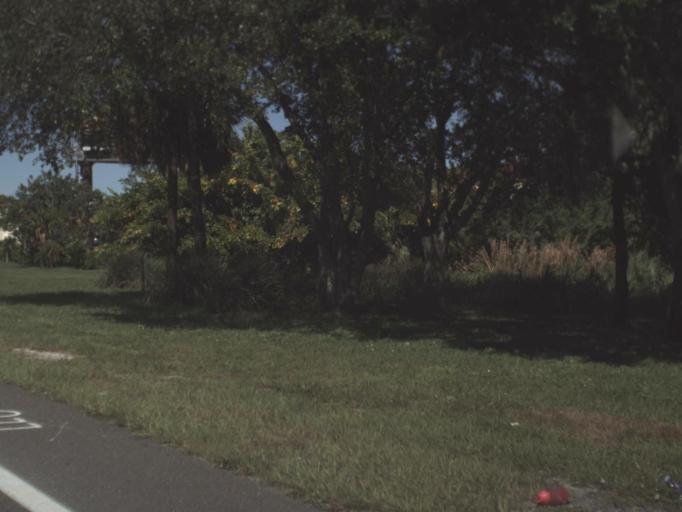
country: US
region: Florida
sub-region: Lee County
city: North Fort Myers
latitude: 26.6585
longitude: -81.8828
